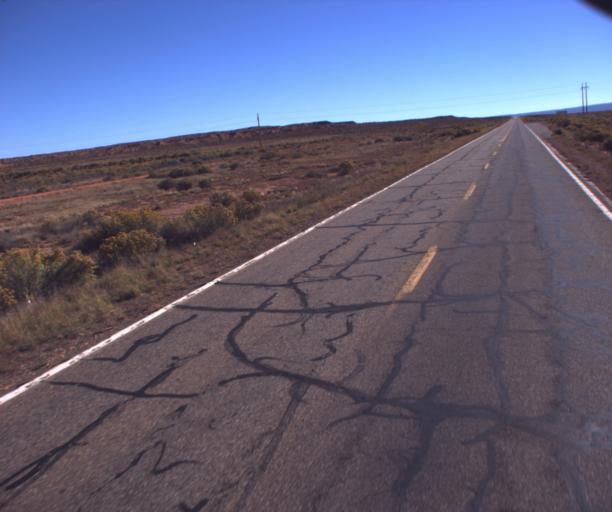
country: US
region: Arizona
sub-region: Coconino County
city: Fredonia
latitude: 36.9350
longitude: -112.5069
